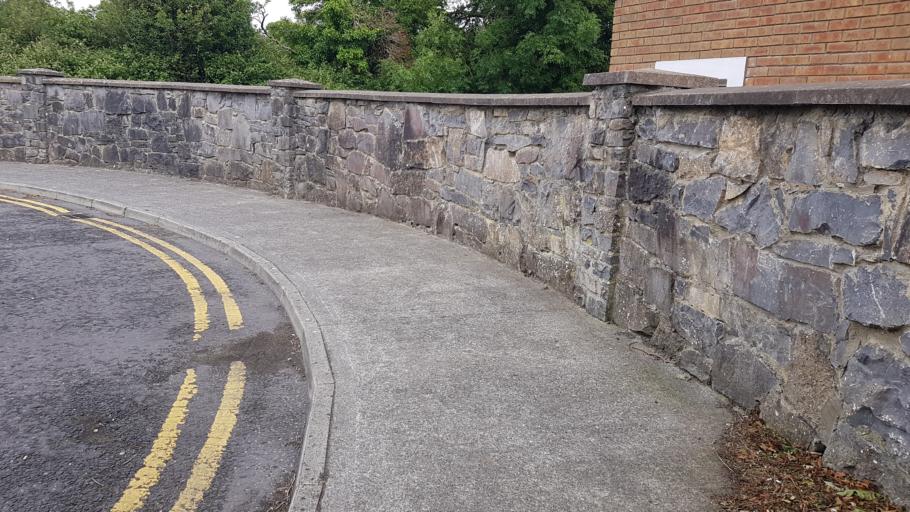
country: IE
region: Connaught
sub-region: County Galway
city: Gaillimh
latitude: 53.2989
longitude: -9.0235
